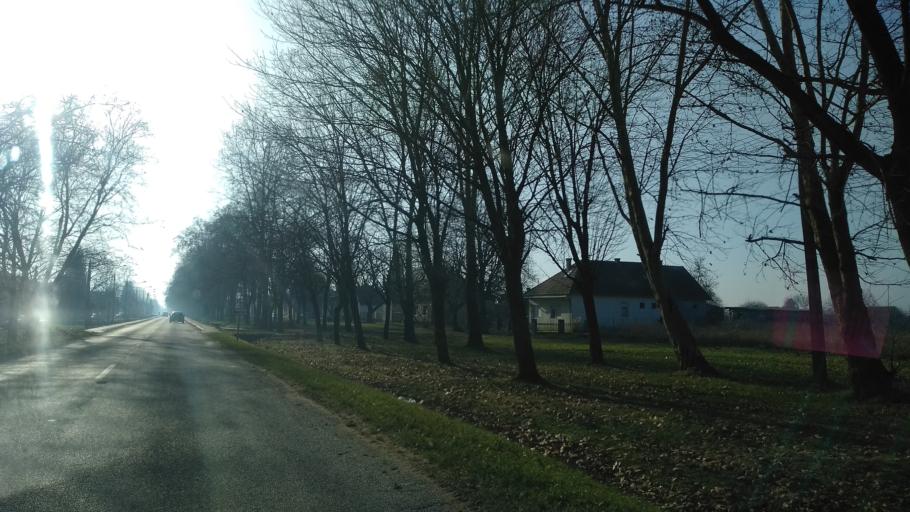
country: HU
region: Somogy
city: Barcs
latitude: 45.9721
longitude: 17.4587
